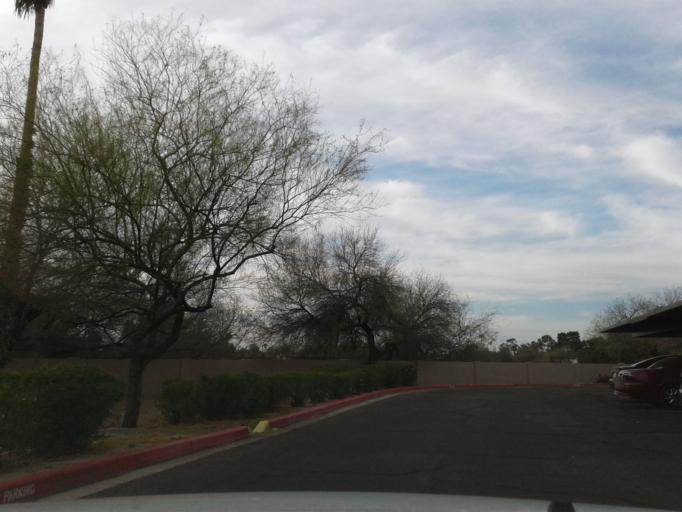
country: US
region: Arizona
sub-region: Maricopa County
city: Paradise Valley
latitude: 33.5860
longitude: -111.9324
